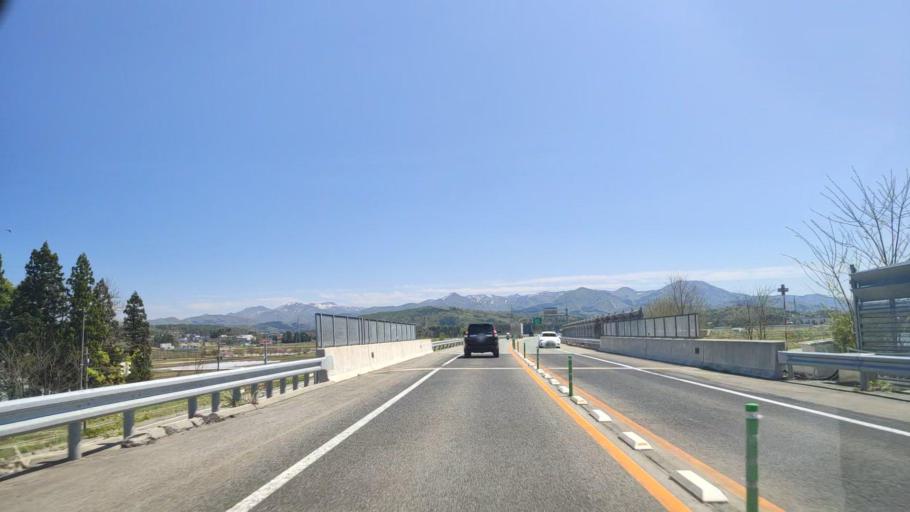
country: JP
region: Yamagata
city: Obanazawa
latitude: 38.6175
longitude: 140.3851
